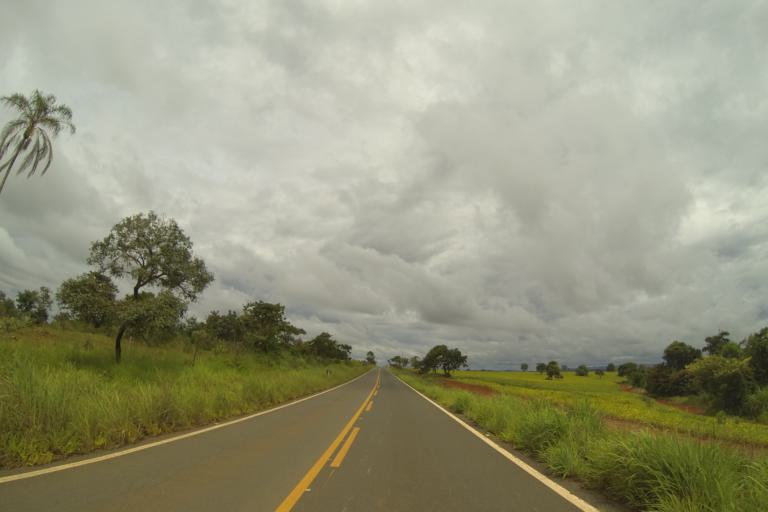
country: BR
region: Minas Gerais
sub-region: Bambui
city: Bambui
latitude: -20.0983
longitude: -46.1215
